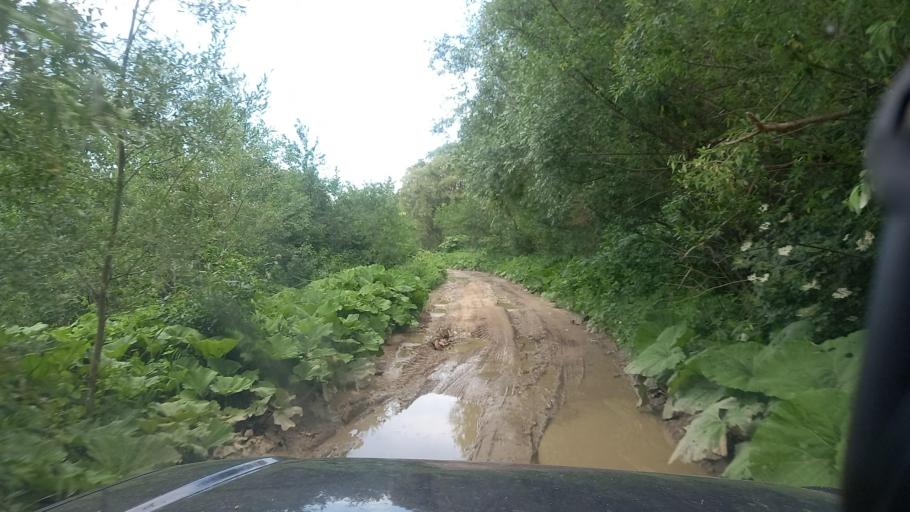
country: RU
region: Krasnodarskiy
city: Peredovaya
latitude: 44.0825
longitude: 41.3552
